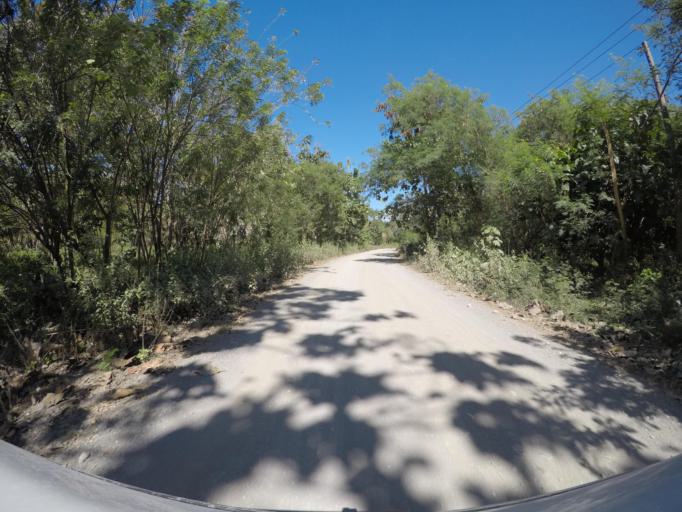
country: TL
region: Viqueque
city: Viqueque
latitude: -8.9742
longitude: 126.0659
